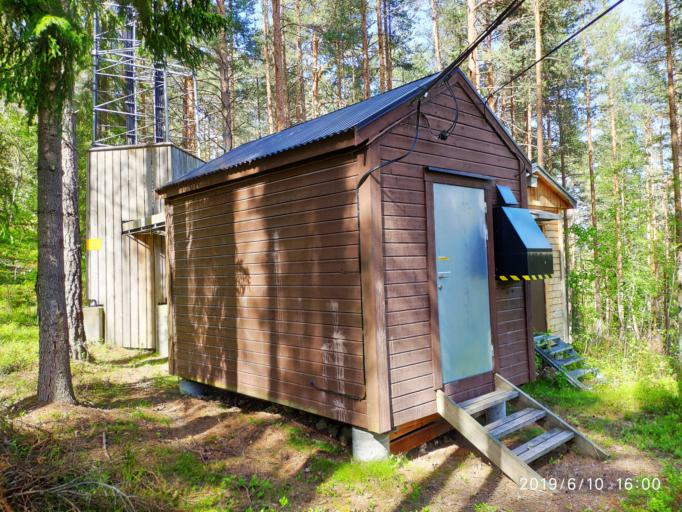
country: NO
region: Oppland
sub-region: Jevnaker
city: Jevnaker
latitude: 60.2506
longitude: 10.3674
